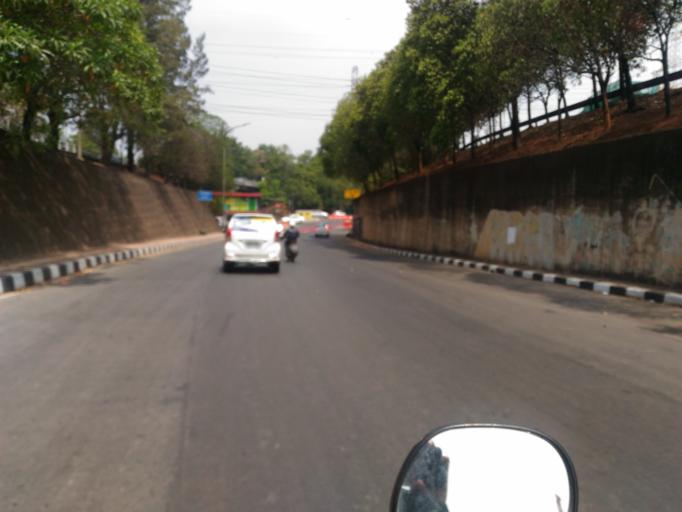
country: ID
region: Jakarta Raya
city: Jakarta
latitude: -6.2465
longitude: 106.8741
